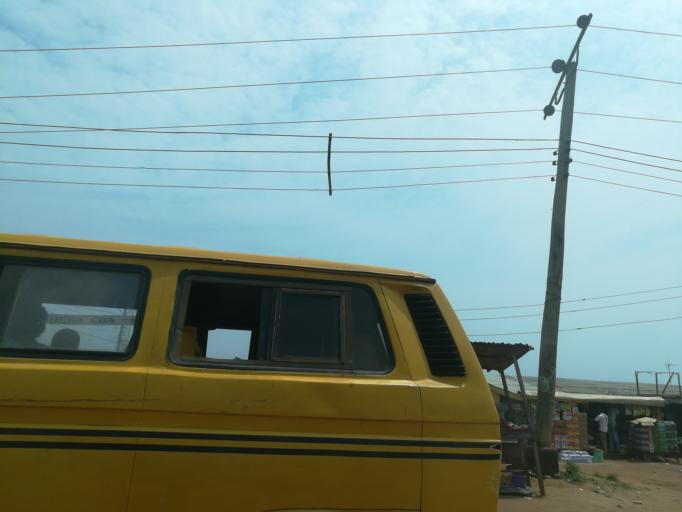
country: NG
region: Lagos
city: Ikorodu
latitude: 6.6026
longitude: 3.6149
